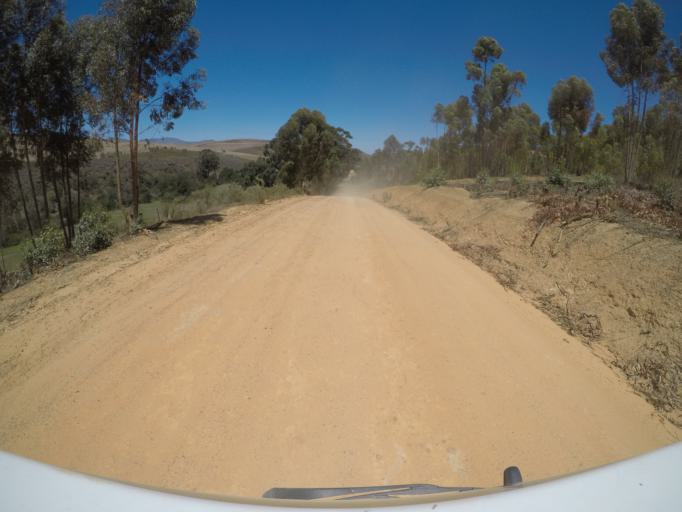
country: ZA
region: Western Cape
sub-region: Overberg District Municipality
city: Caledon
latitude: -34.1992
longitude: 19.2208
